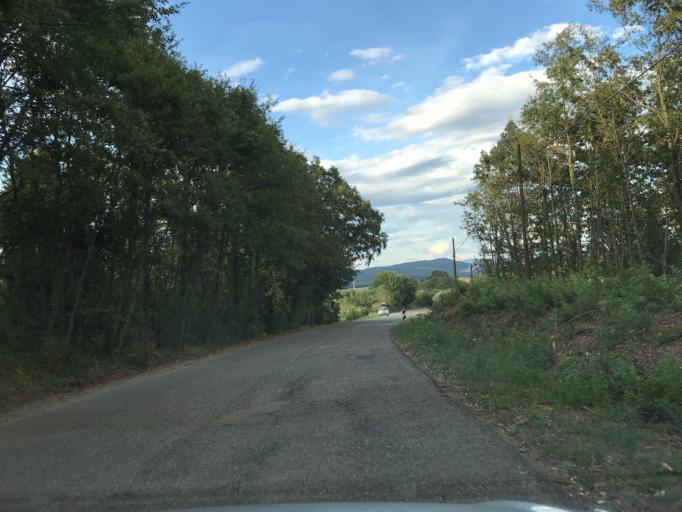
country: IT
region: Umbria
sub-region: Provincia di Terni
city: Avigliano Umbro
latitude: 42.6497
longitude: 12.3609
